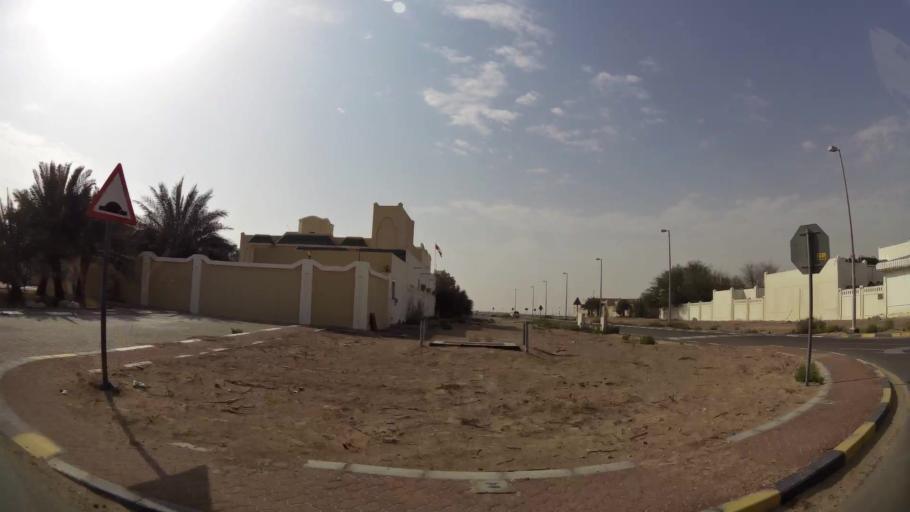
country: AE
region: Abu Dhabi
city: Abu Dhabi
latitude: 24.2772
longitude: 54.6900
